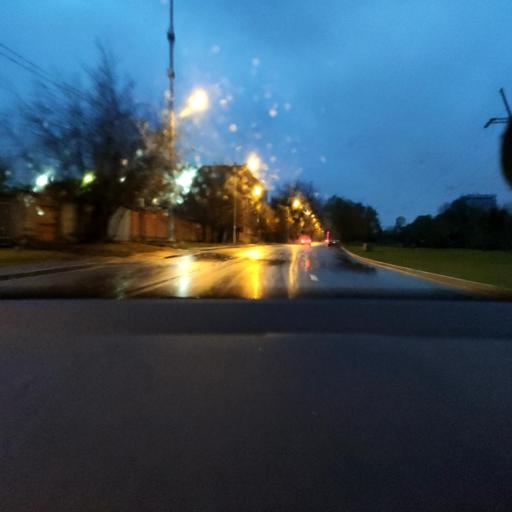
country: RU
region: Moscow
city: Zapadnoye Degunino
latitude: 55.8522
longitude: 37.5428
